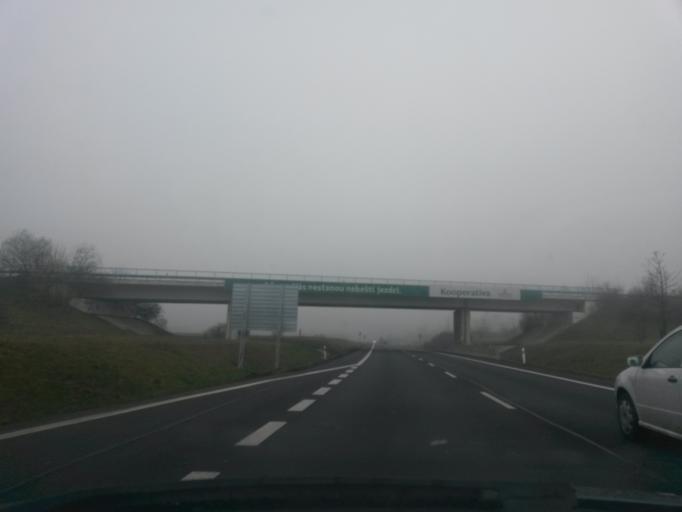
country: CZ
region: Ustecky
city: Cerncice
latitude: 50.3390
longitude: 13.8283
